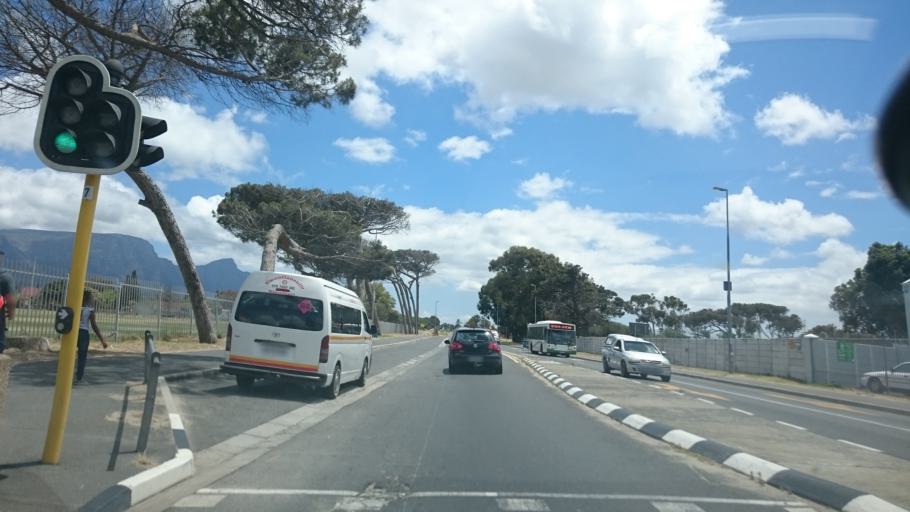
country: ZA
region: Western Cape
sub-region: City of Cape Town
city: Bergvliet
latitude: -34.0601
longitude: 18.4600
